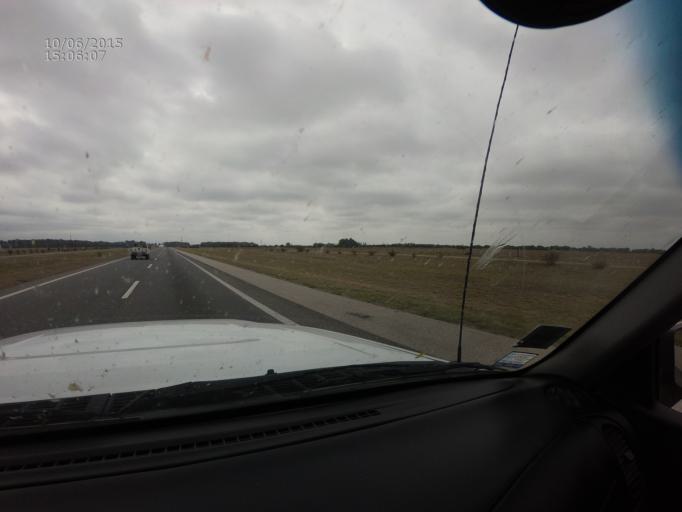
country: AR
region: Cordoba
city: Pilar
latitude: -31.6879
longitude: -63.8325
